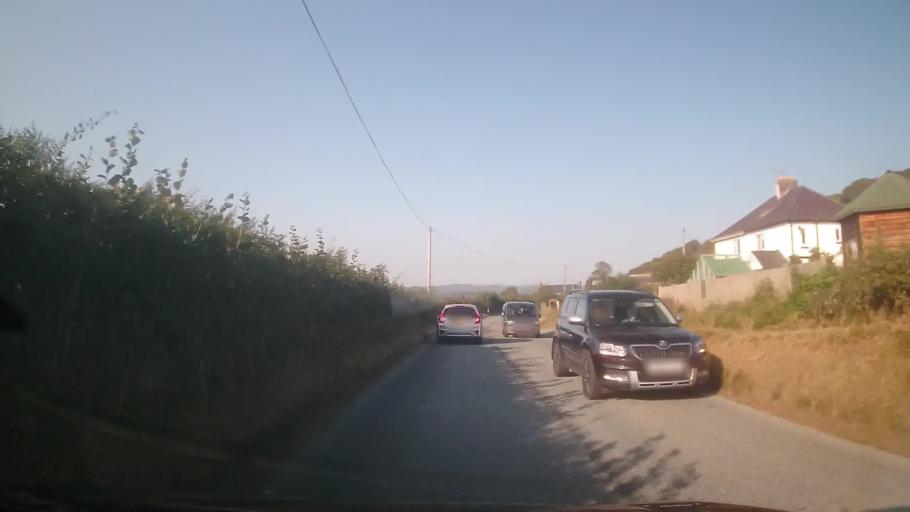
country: GB
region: Wales
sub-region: County of Ceredigion
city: Lledrod
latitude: 52.2328
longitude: -3.9312
